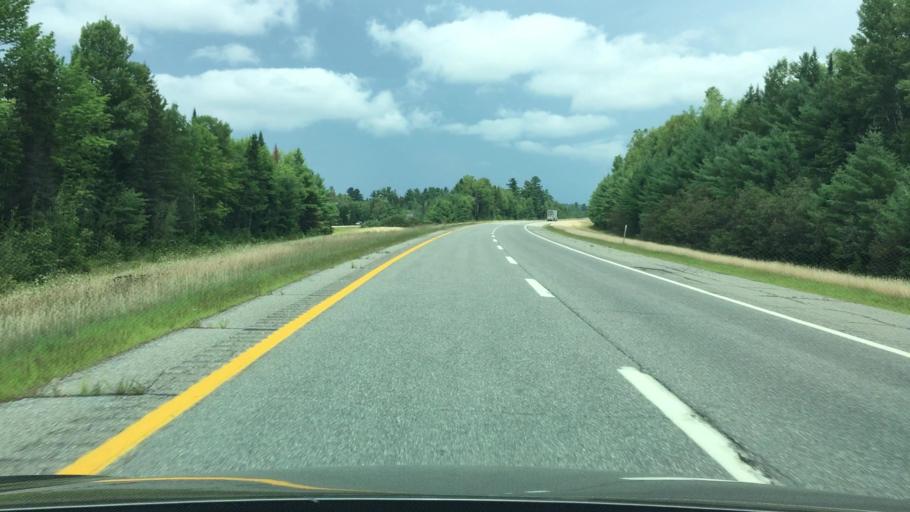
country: US
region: Maine
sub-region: Penobscot County
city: Lincoln
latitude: 45.3848
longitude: -68.6043
